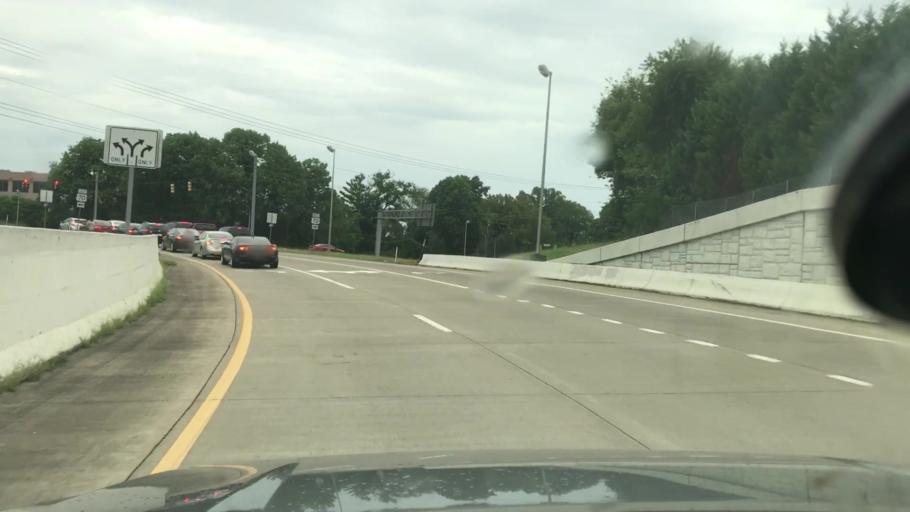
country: US
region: Tennessee
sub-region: Davidson County
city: Lakewood
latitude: 36.1691
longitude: -86.6899
